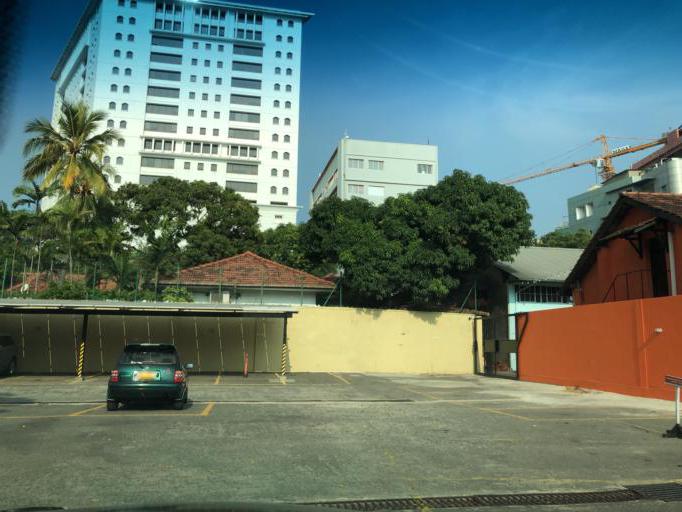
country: LK
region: Western
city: Colombo
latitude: 6.9165
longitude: 79.8583
